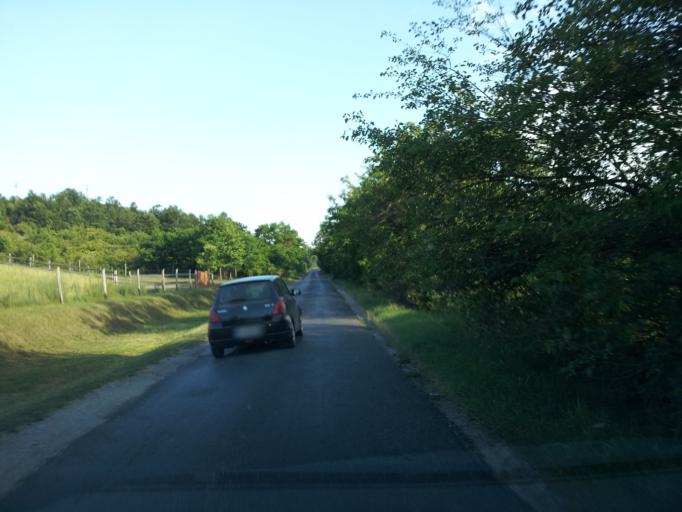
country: HU
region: Fejer
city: Many
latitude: 47.5455
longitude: 18.5882
